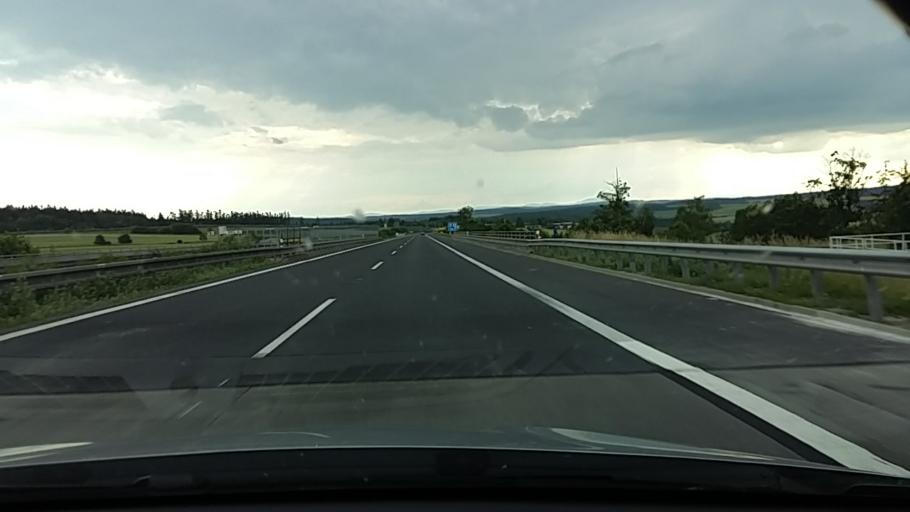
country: CZ
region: Plzensky
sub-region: Okres Tachov
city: Kladruby
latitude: 49.7046
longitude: 13.0022
